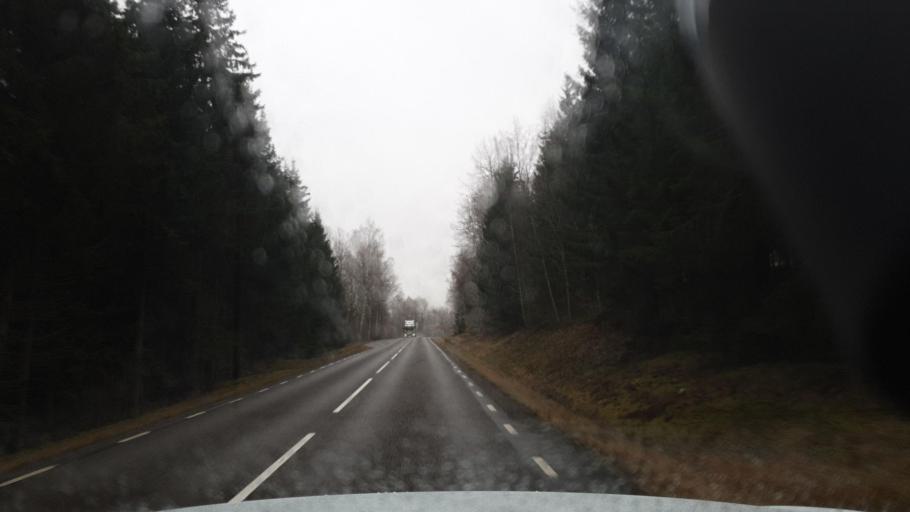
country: SE
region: Vaermland
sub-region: Eda Kommun
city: Amotfors
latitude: 59.7239
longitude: 12.4252
